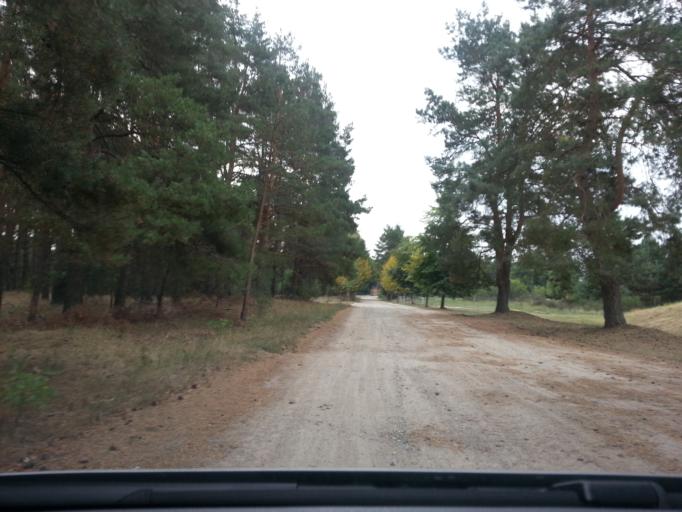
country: DE
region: Mecklenburg-Vorpommern
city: Ferdinandshof
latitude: 53.7102
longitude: 13.9437
